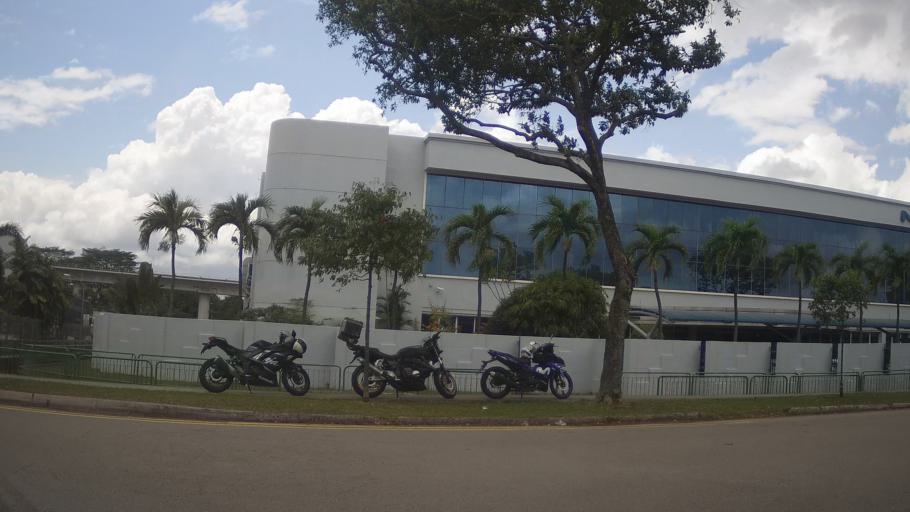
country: MY
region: Johor
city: Johor Bahru
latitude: 1.3242
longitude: 103.6667
